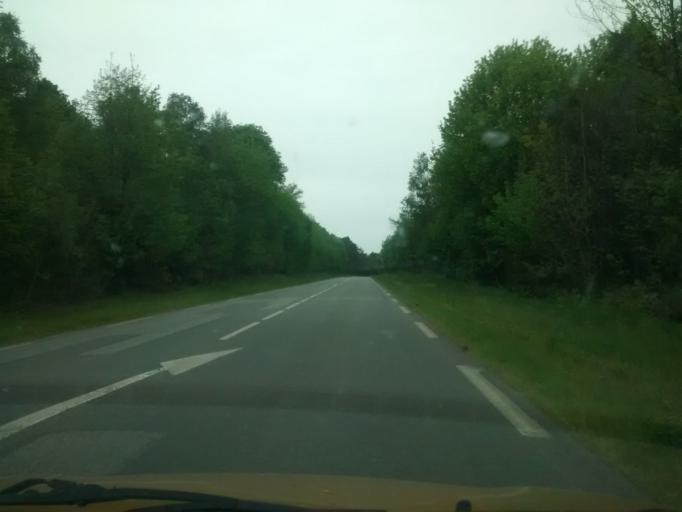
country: FR
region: Brittany
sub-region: Departement du Morbihan
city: Molac
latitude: 47.7657
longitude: -2.4490
